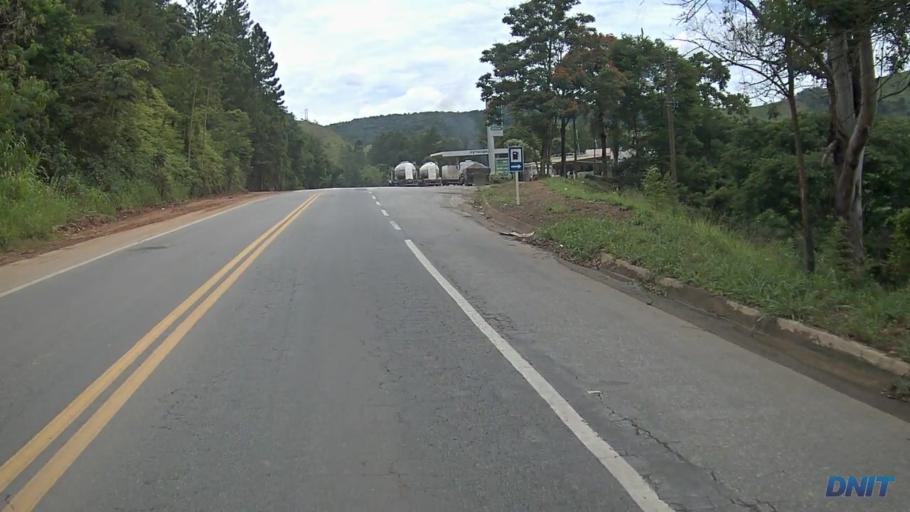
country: BR
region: Minas Gerais
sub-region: Nova Era
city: Nova Era
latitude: -19.7299
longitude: -43.0153
